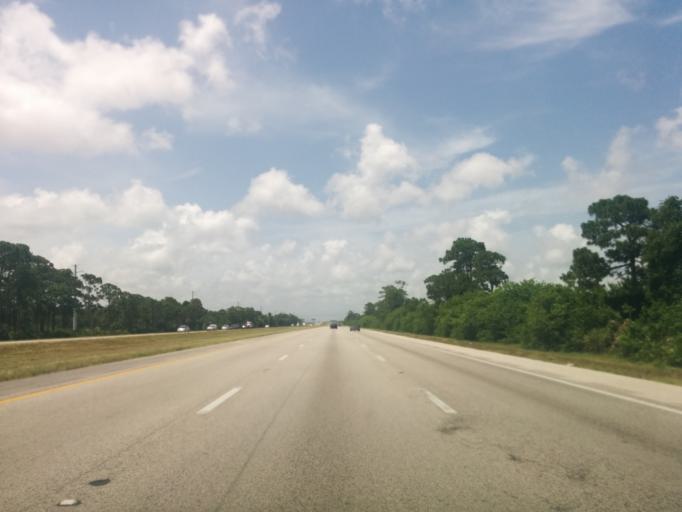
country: US
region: Florida
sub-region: Saint Lucie County
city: River Park
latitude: 27.3392
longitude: -80.4140
